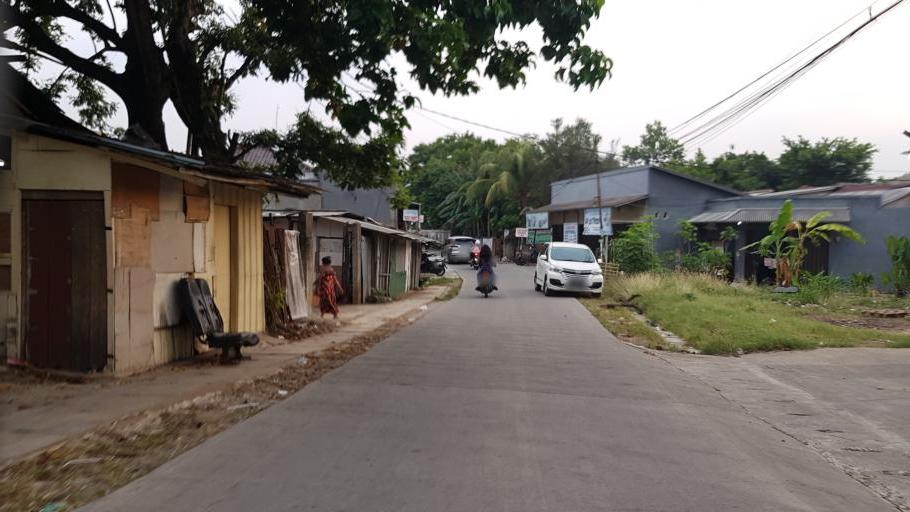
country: ID
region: West Java
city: Depok
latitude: -6.3784
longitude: 106.8061
